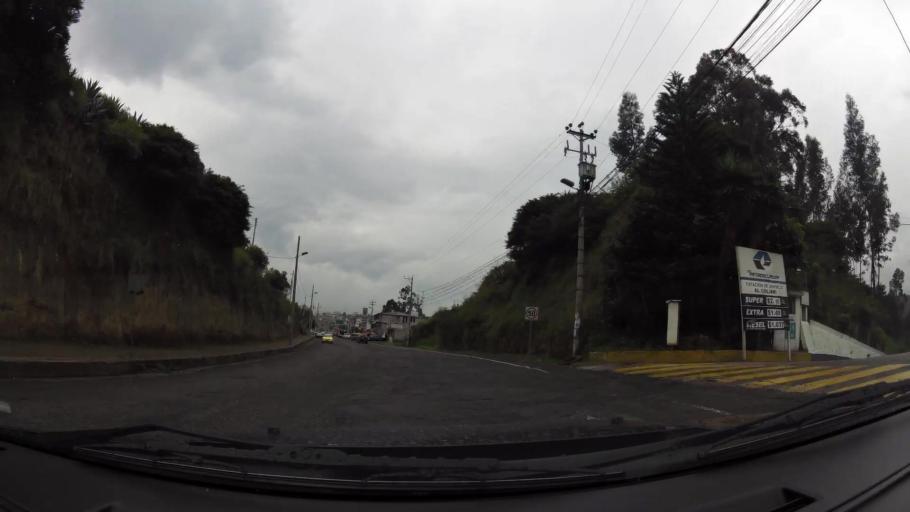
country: EC
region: Pichincha
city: Sangolqui
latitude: -0.3339
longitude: -78.4368
